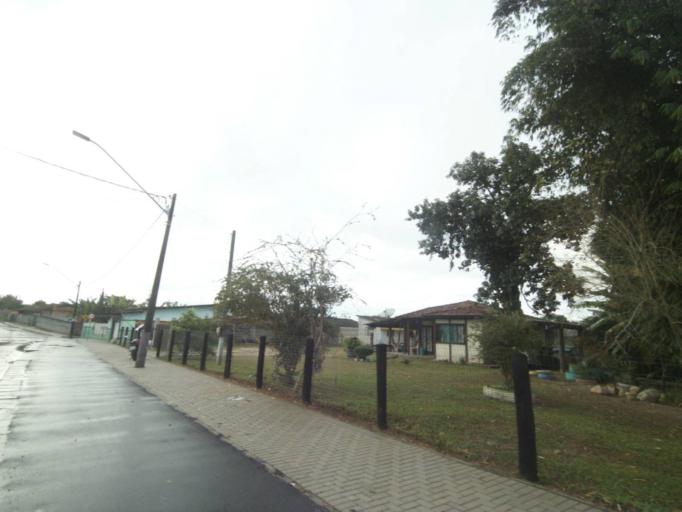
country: BR
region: Parana
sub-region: Paranagua
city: Paranagua
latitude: -25.5734
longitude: -48.5709
